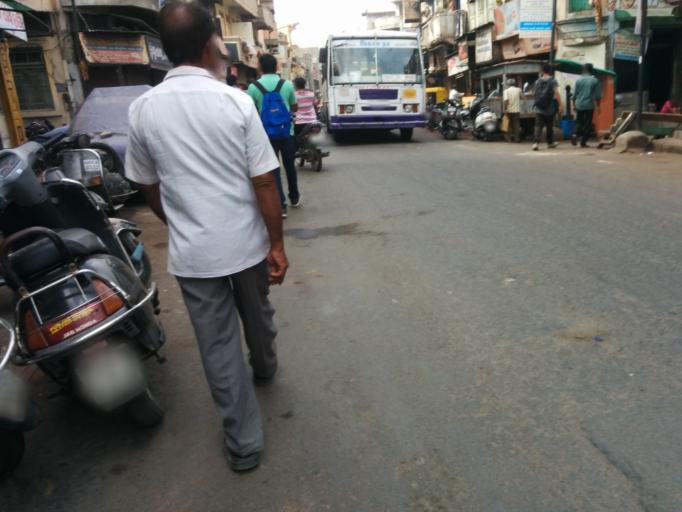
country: IN
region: Gujarat
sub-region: Ahmadabad
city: Ahmedabad
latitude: 23.0194
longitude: 72.5943
